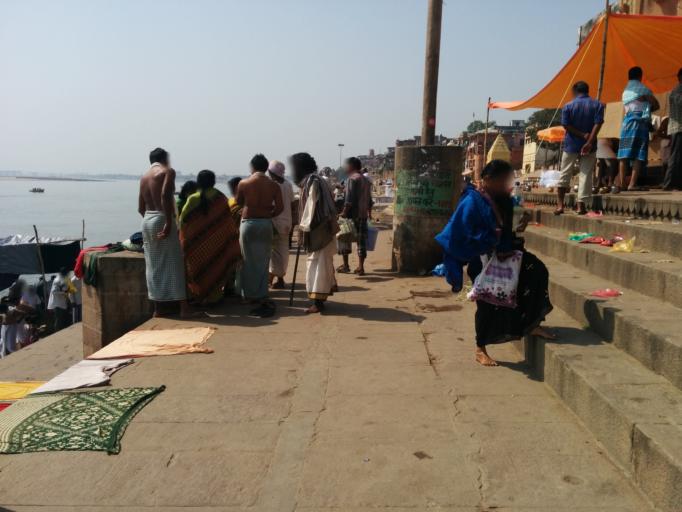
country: IN
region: Uttar Pradesh
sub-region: Varanasi
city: Varanasi
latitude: 25.3025
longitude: 83.0080
